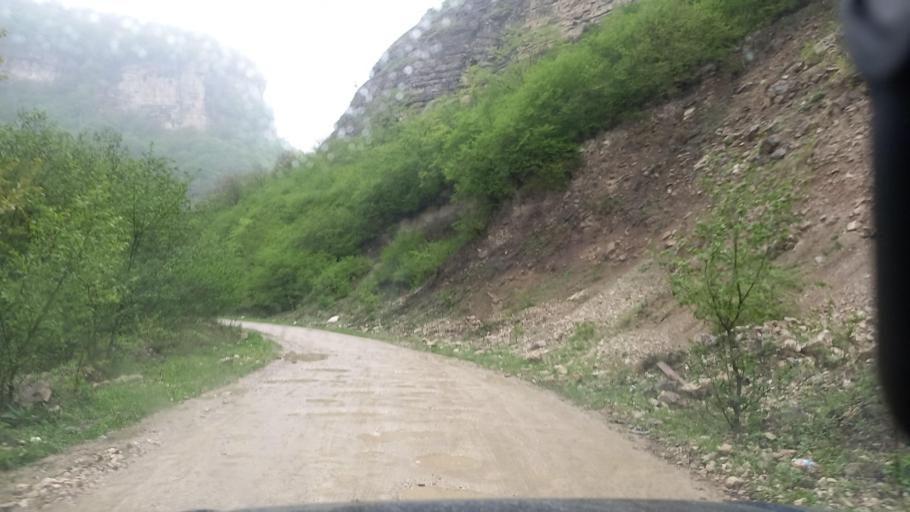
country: RU
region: Kabardino-Balkariya
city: Gundelen
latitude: 43.5930
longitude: 43.1315
